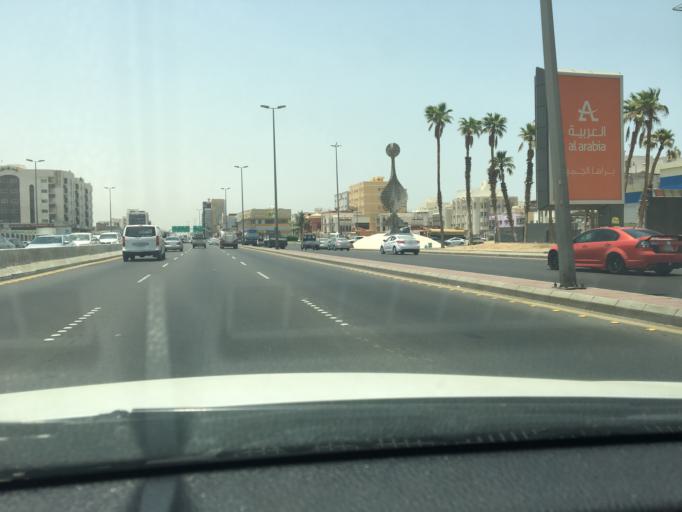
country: SA
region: Makkah
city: Jeddah
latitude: 21.5536
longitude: 39.1884
